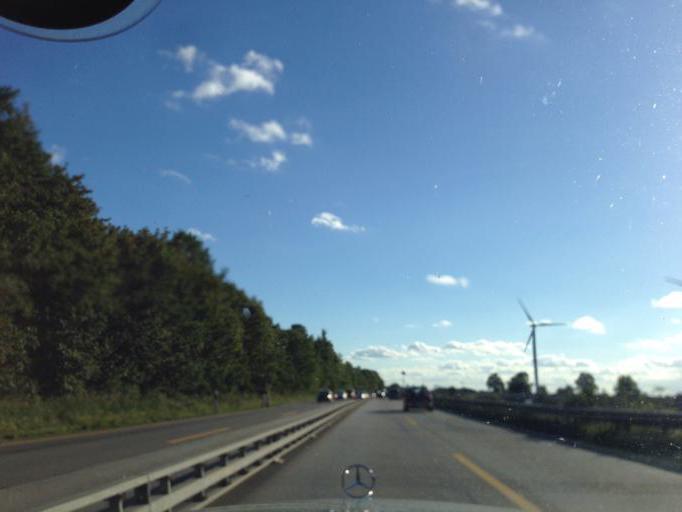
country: DE
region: Schleswig-Holstein
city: Loop
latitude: 54.1338
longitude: 9.9599
